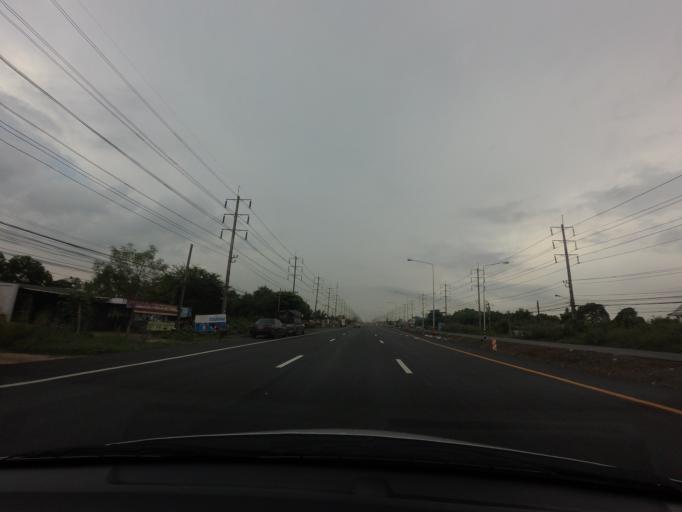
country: TH
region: Bangkok
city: Nong Chok
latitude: 13.8082
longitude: 100.8254
